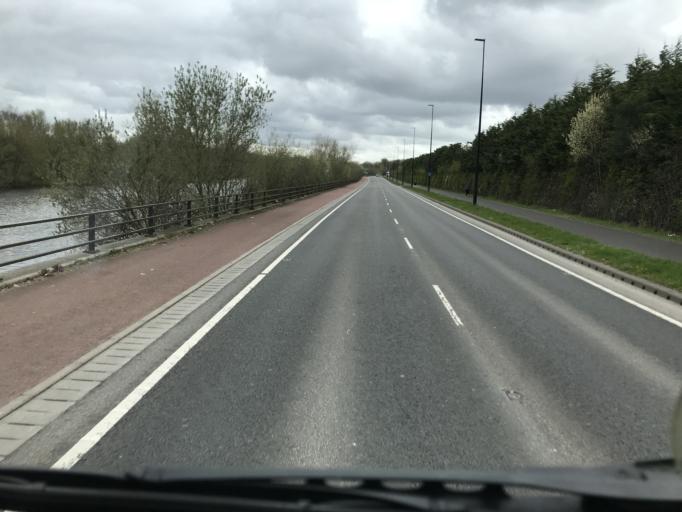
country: GB
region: England
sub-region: Trafford
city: Partington
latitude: 53.4206
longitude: -2.4393
